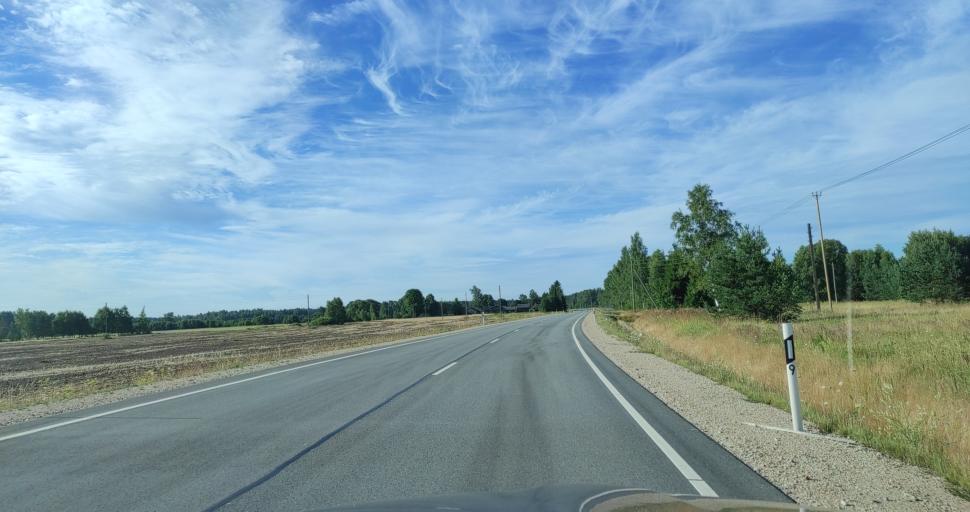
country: LV
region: Pavilostas
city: Pavilosta
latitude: 56.8181
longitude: 21.2275
